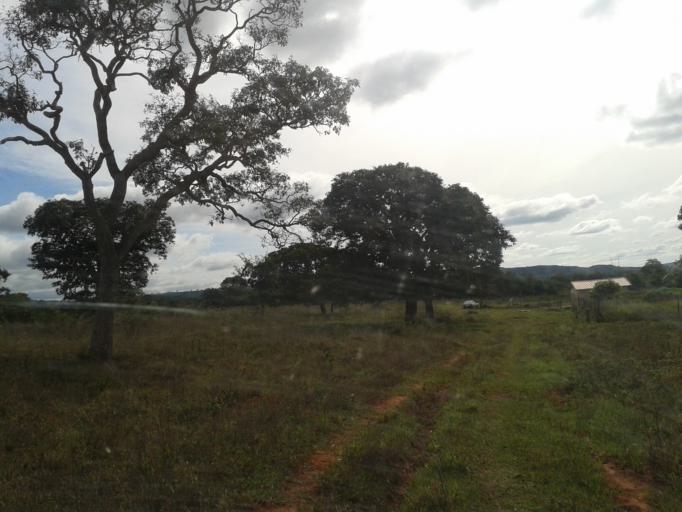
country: BR
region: Minas Gerais
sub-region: Campina Verde
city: Campina Verde
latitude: -19.4266
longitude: -49.7293
